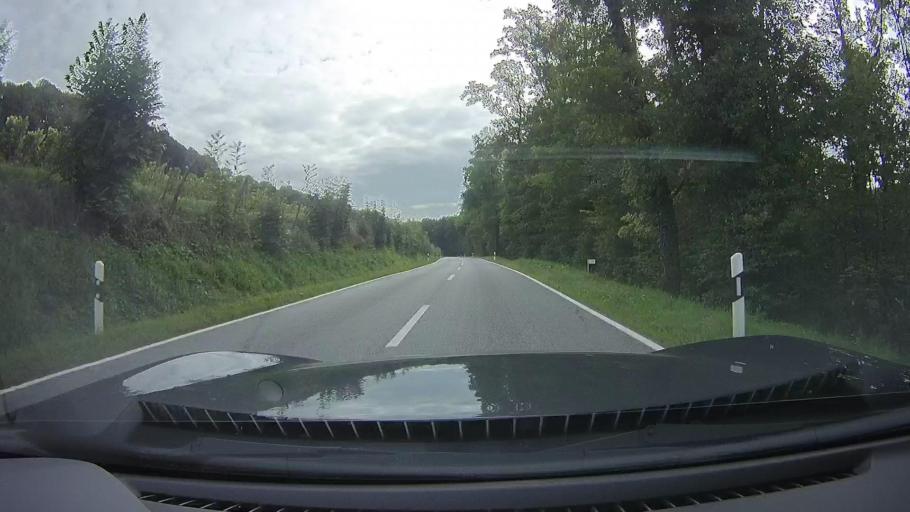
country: DE
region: Baden-Wuerttemberg
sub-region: Regierungsbezirk Stuttgart
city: Lowenstein
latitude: 49.0867
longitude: 9.3631
